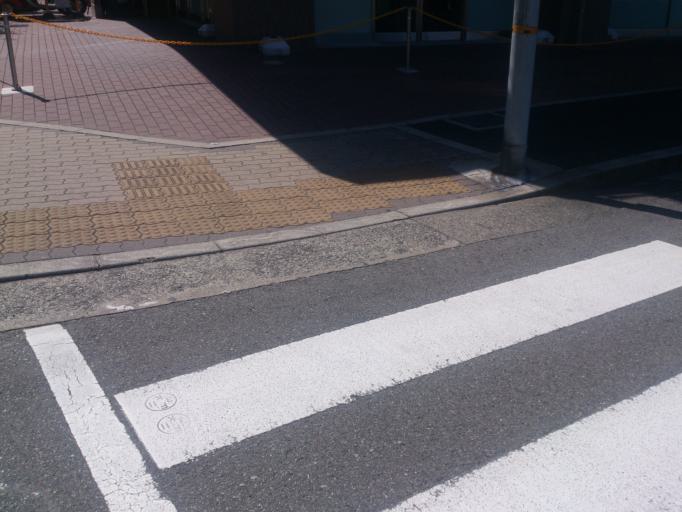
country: JP
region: Hyogo
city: Amagasaki
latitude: 34.7312
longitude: 135.4307
